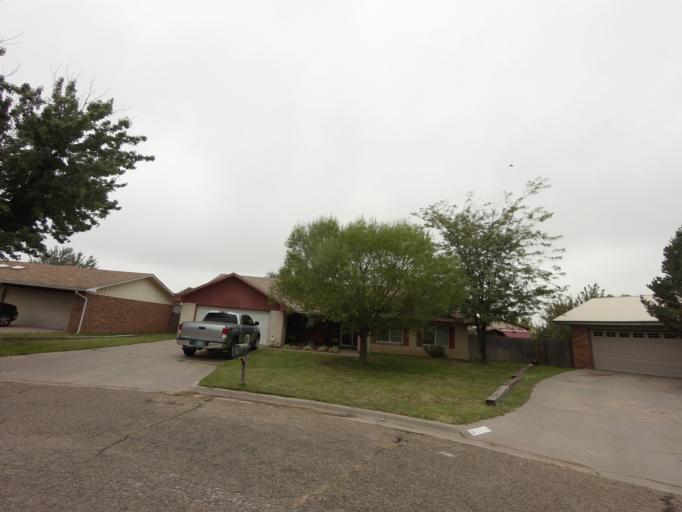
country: US
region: New Mexico
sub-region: Curry County
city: Clovis
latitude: 34.4378
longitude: -103.1933
